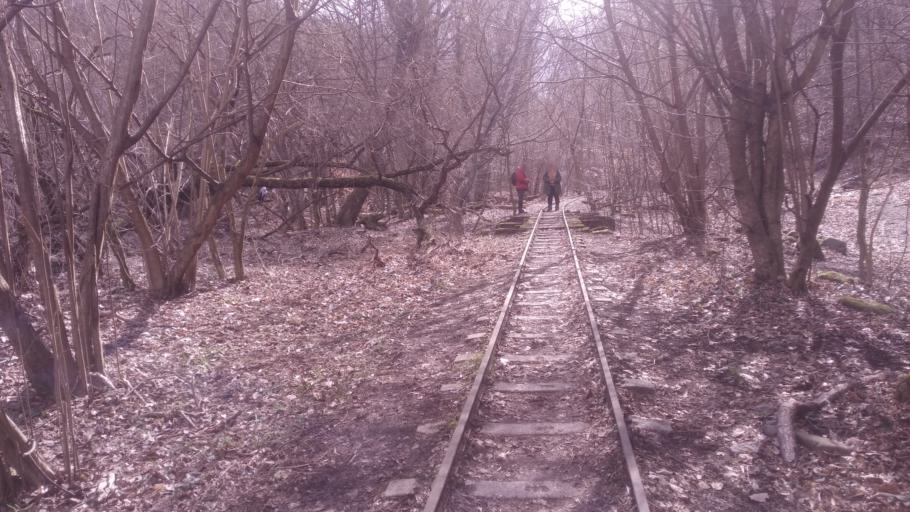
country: SK
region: Nitriansky
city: Sahy
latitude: 47.9763
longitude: 18.8952
